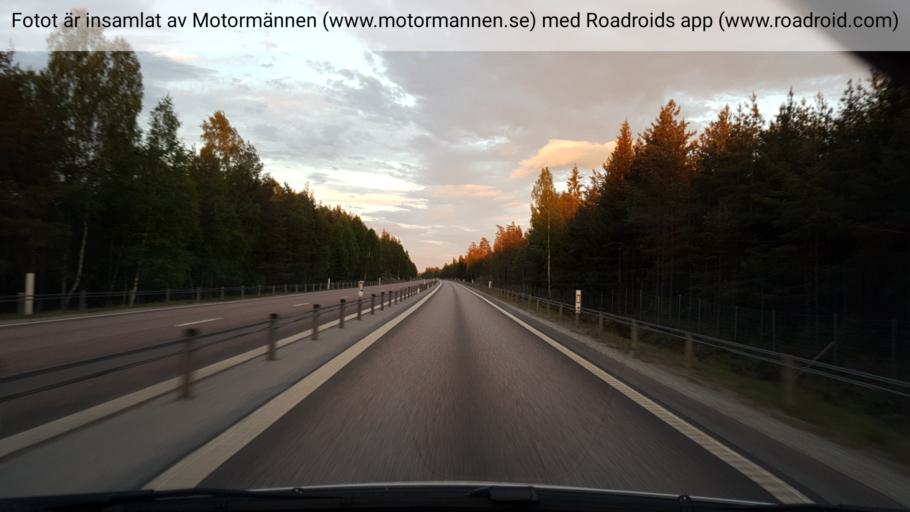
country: SE
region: Vaestmanland
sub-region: Surahammars Kommun
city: Ramnas
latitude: 59.8277
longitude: 16.0899
